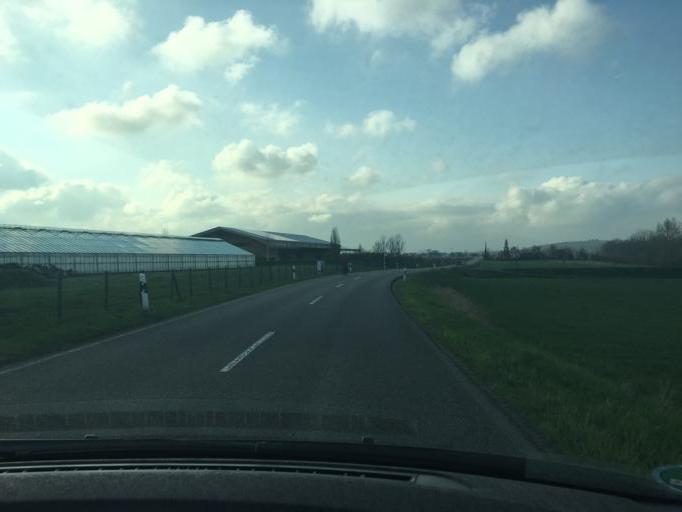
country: DE
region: North Rhine-Westphalia
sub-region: Regierungsbezirk Koln
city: Weilerswist
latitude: 50.7243
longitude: 6.9042
